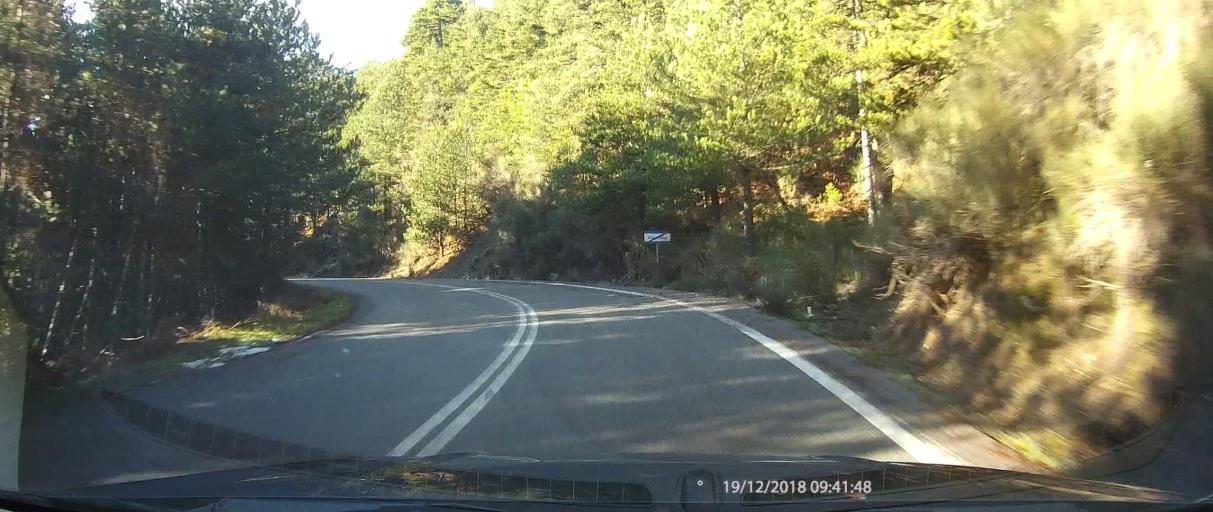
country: GR
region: Peloponnese
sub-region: Nomos Messinias
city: Paralia Vergas
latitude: 37.0692
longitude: 22.2692
